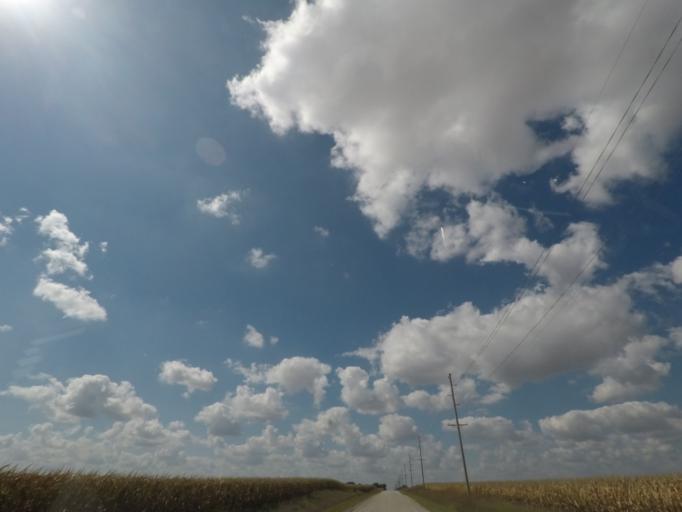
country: US
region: Iowa
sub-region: Story County
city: Nevada
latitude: 42.0344
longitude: -93.3996
